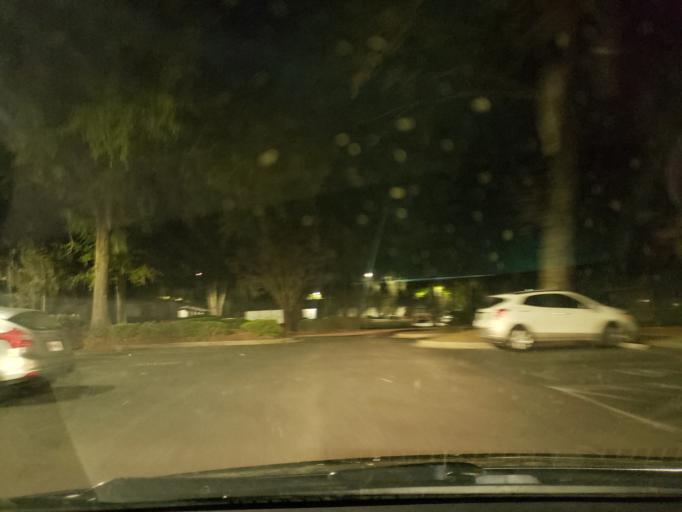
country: US
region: Georgia
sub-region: Chatham County
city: Montgomery
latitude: 31.9799
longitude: -81.1289
